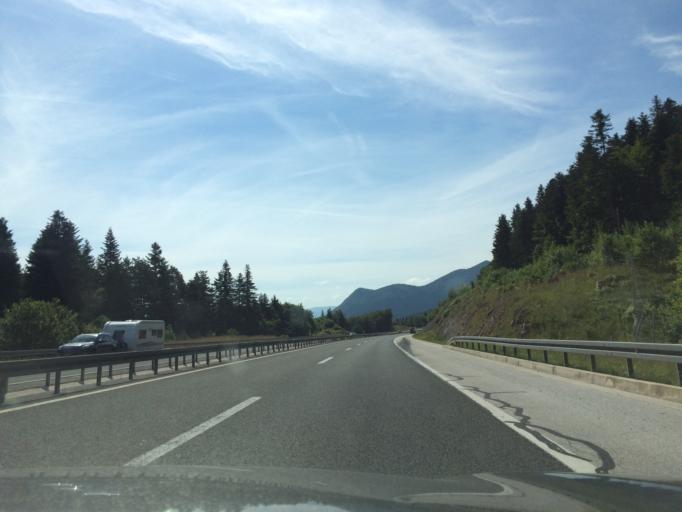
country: HR
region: Licko-Senjska
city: Otocac
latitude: 44.8456
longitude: 15.2390
